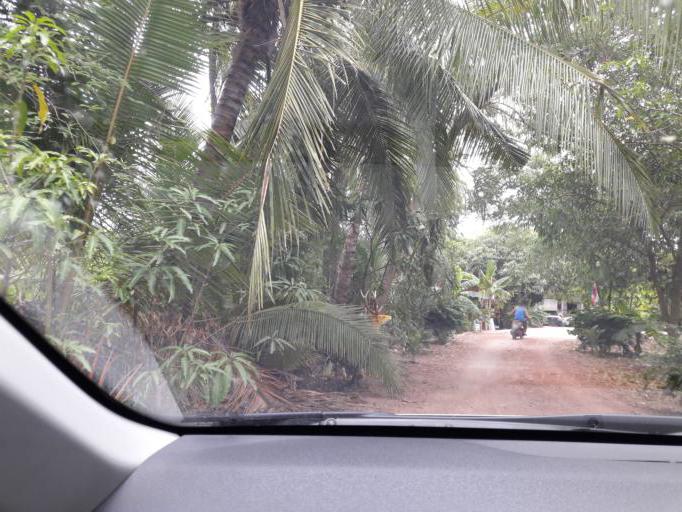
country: TH
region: Ratchaburi
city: Damnoen Saduak
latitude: 13.5437
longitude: 100.0087
